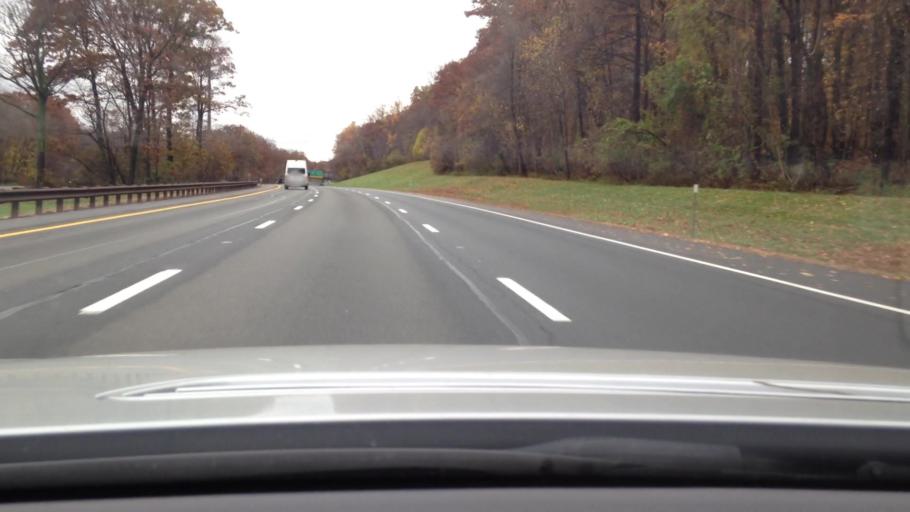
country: US
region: New Jersey
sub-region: Bergen County
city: Ho-Ho-Kus
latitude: 40.9885
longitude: -74.0734
